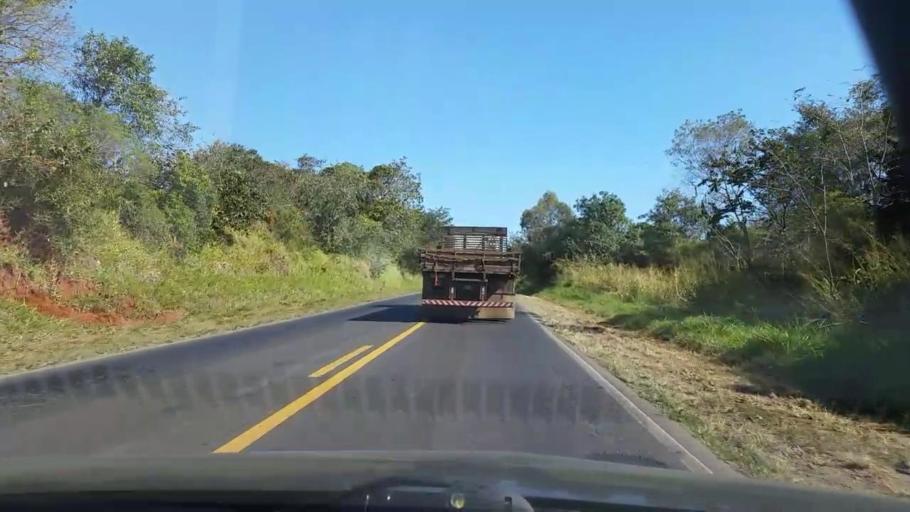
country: BR
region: Sao Paulo
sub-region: Sao Manuel
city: Sao Manuel
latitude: -22.8117
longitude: -48.6774
